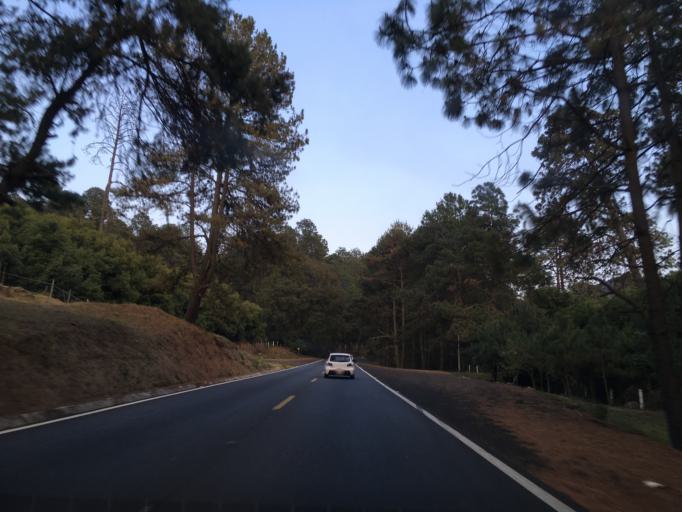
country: MX
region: Michoacan
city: Tingambato
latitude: 19.4957
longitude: -101.8252
